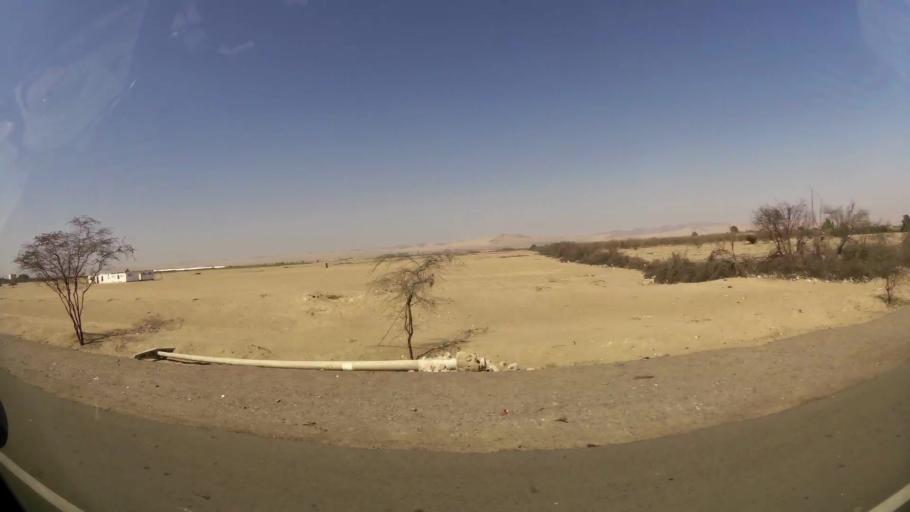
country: PE
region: Ica
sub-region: Provincia de Ica
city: Guadalupe
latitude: -13.9320
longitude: -75.9088
